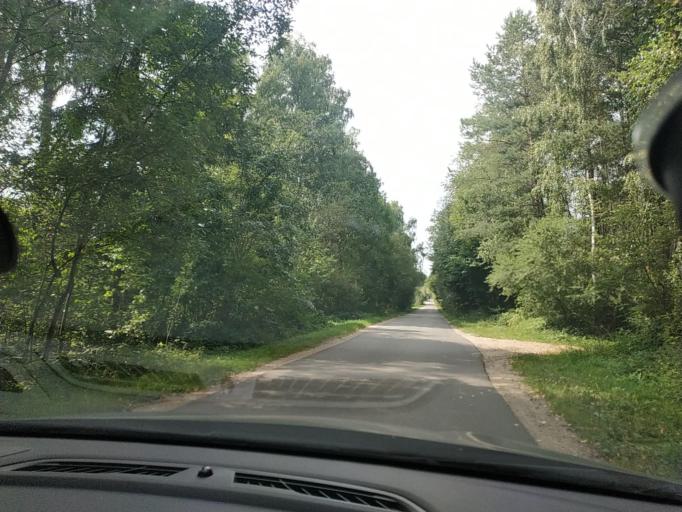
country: LT
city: Nemencine
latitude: 54.8527
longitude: 25.4480
